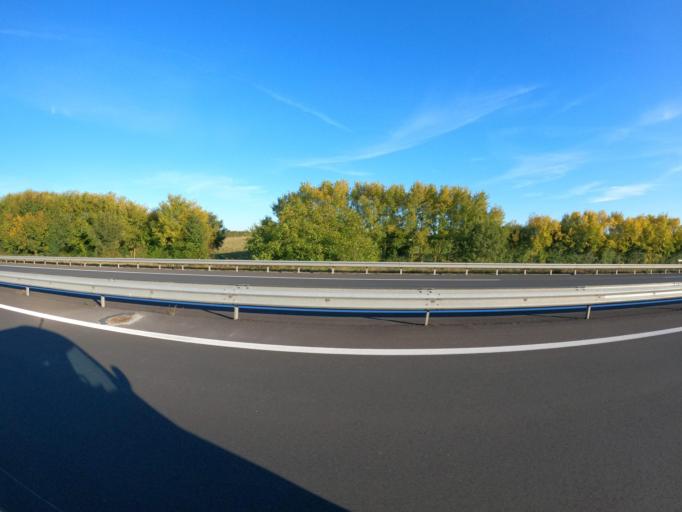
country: FR
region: Pays de la Loire
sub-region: Departement de la Vendee
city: Saint-Fulgent
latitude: 46.8401
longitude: -1.1534
